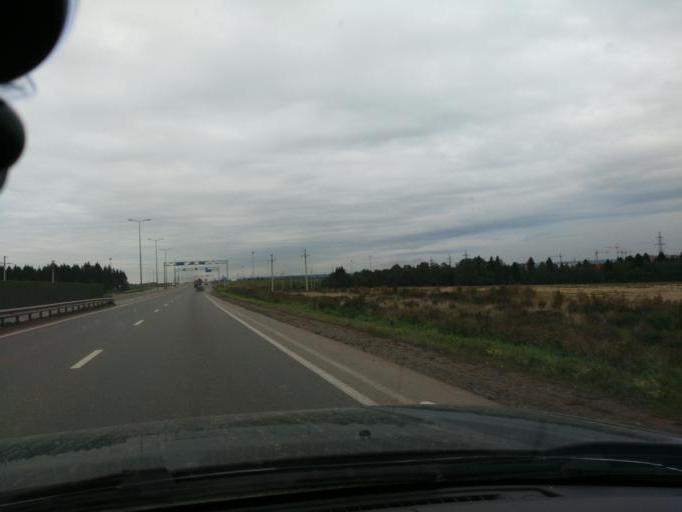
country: RU
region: Perm
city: Froly
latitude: 57.9336
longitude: 56.2562
